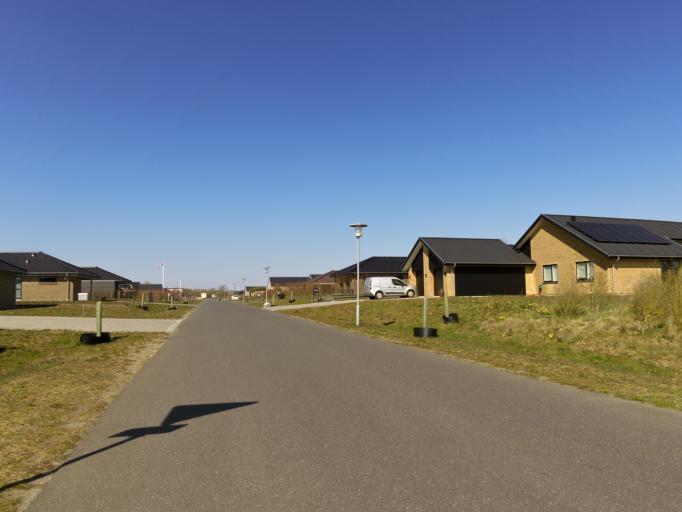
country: DK
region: South Denmark
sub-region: Esbjerg Kommune
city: Ribe
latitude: 55.3378
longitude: 8.7952
